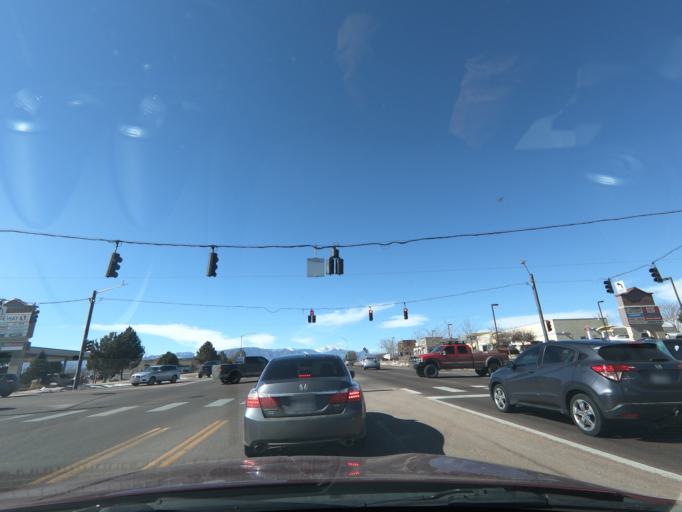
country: US
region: Colorado
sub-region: El Paso County
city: Security-Widefield
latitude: 38.7181
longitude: -104.6975
